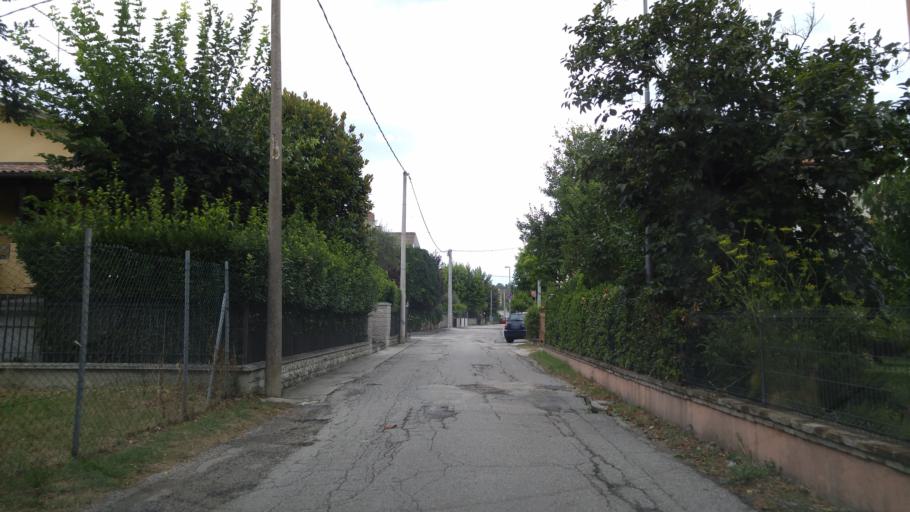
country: IT
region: The Marches
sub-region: Provincia di Pesaro e Urbino
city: Fano
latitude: 43.8474
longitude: 13.0046
